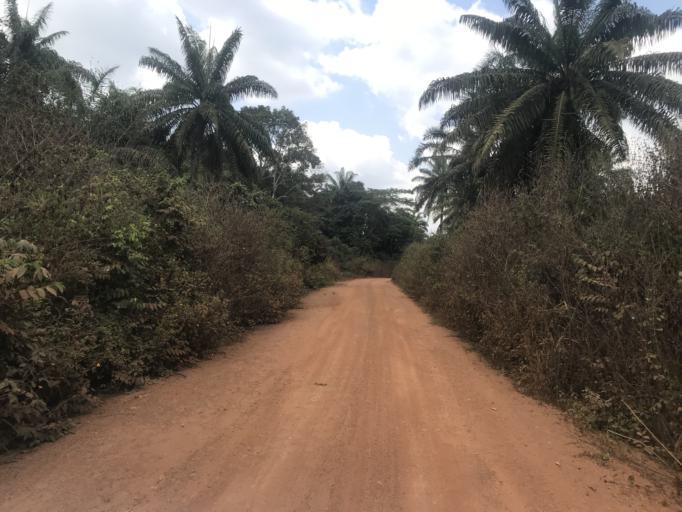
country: NG
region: Osun
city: Inisa
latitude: 7.8668
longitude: 4.3835
